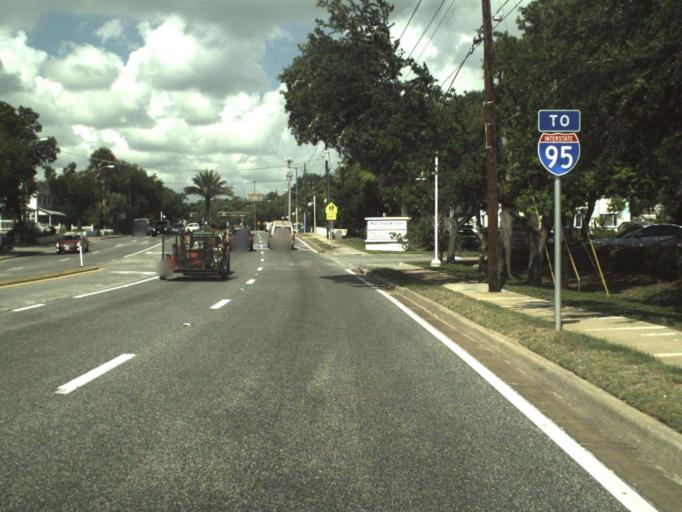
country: US
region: Florida
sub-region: Volusia County
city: Port Orange
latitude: 29.1433
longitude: -80.9890
